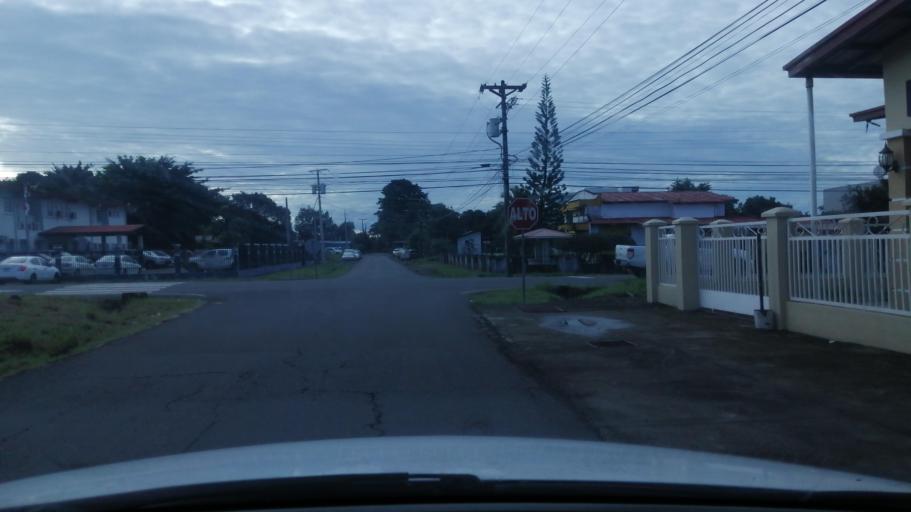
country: PA
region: Chiriqui
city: Mata del Nance
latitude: 8.4534
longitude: -82.4213
